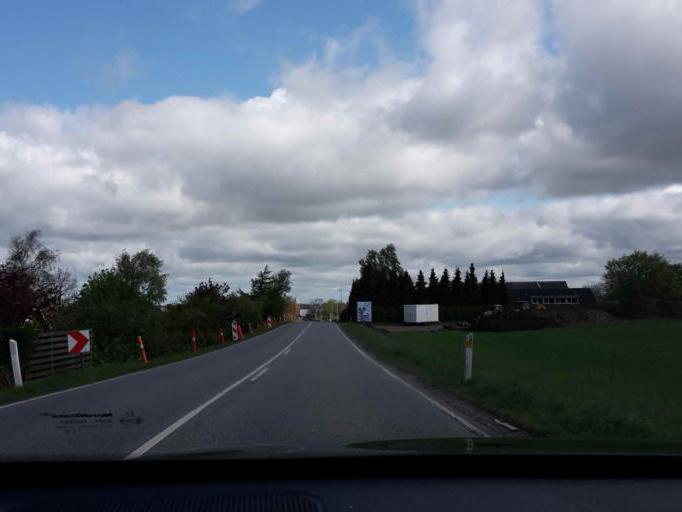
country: DK
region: Central Jutland
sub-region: Syddjurs Kommune
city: Hornslet
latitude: 56.3074
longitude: 10.3167
